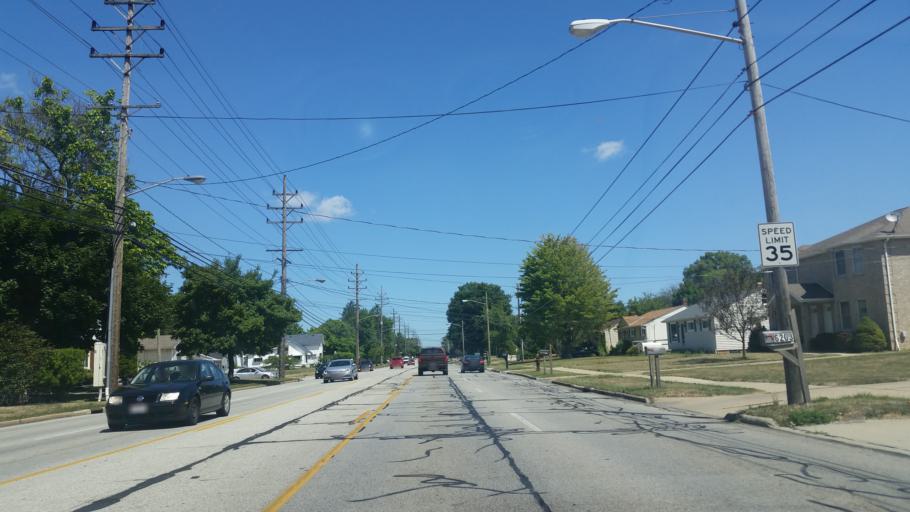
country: US
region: Ohio
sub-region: Cuyahoga County
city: Brook Park
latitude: 41.3958
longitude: -81.7843
